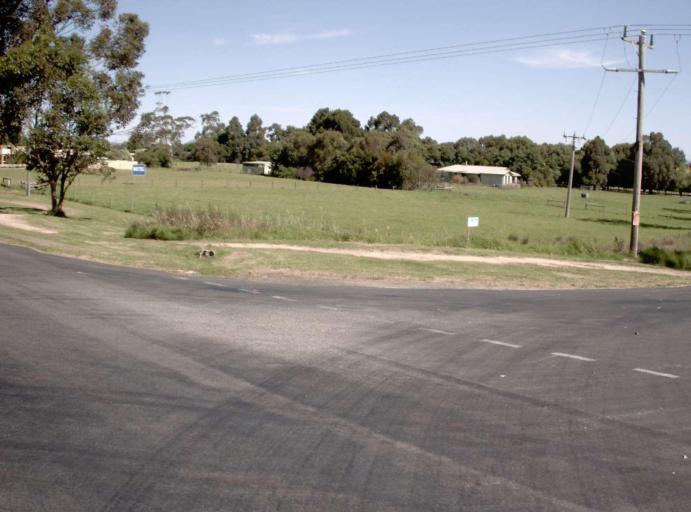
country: AU
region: Victoria
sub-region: Latrobe
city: Morwell
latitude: -38.6590
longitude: 146.3201
